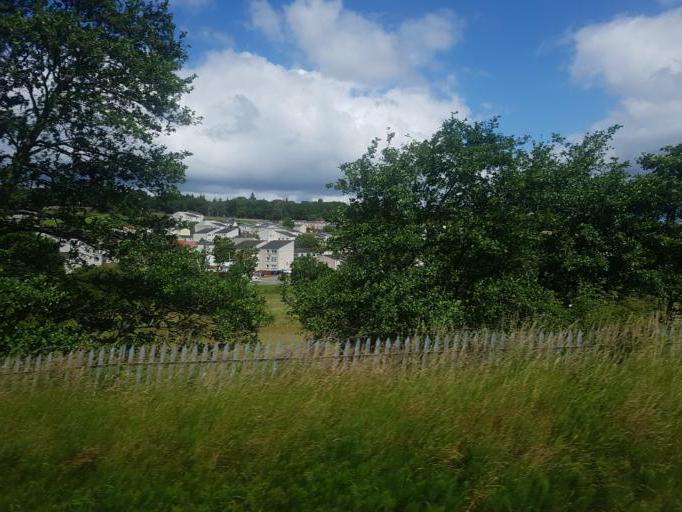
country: GB
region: Scotland
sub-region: Falkirk
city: Falkirk
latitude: 55.9836
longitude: -3.7674
